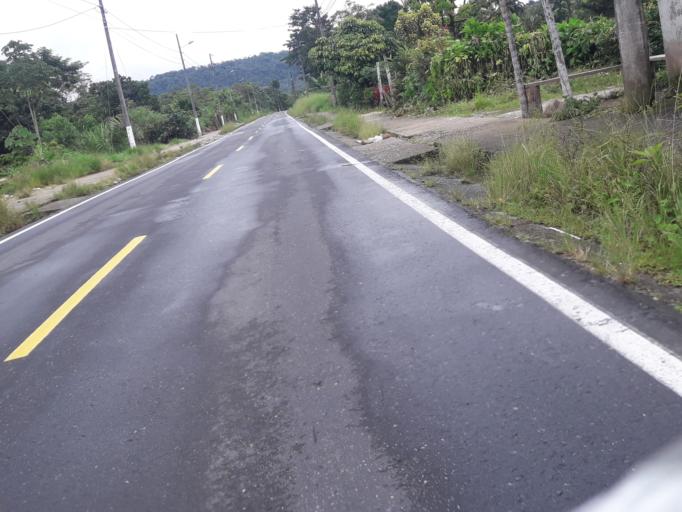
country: EC
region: Napo
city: Tena
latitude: -0.9730
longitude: -77.8549
